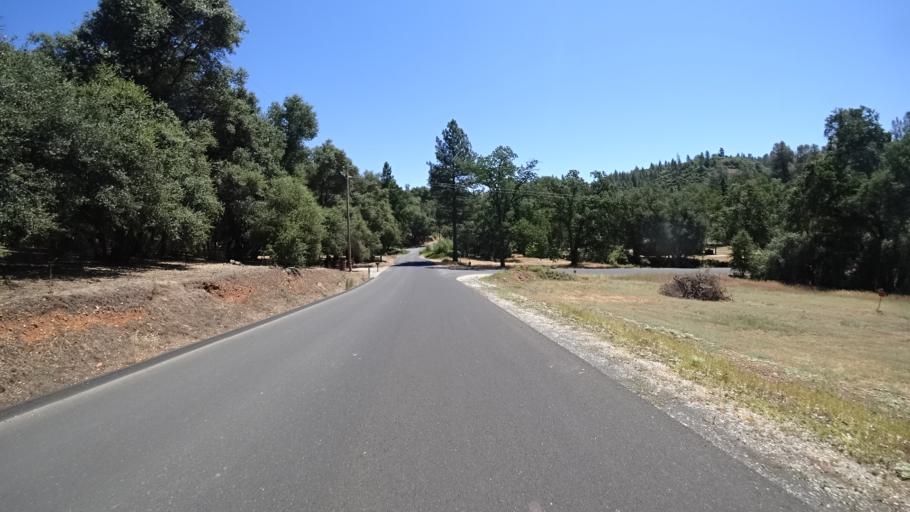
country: US
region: California
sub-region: Calaveras County
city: Murphys
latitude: 38.1296
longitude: -120.4320
